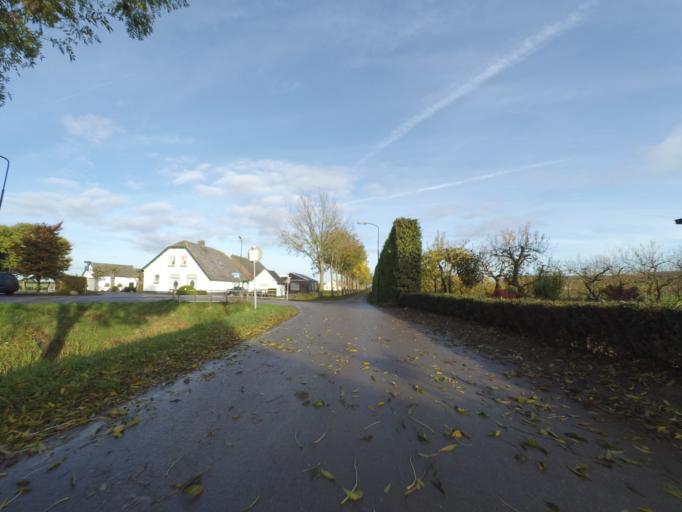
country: NL
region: Utrecht
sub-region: Gemeente Wijk bij Duurstede
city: Wijk bij Duurstede
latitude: 51.9888
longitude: 5.2816
